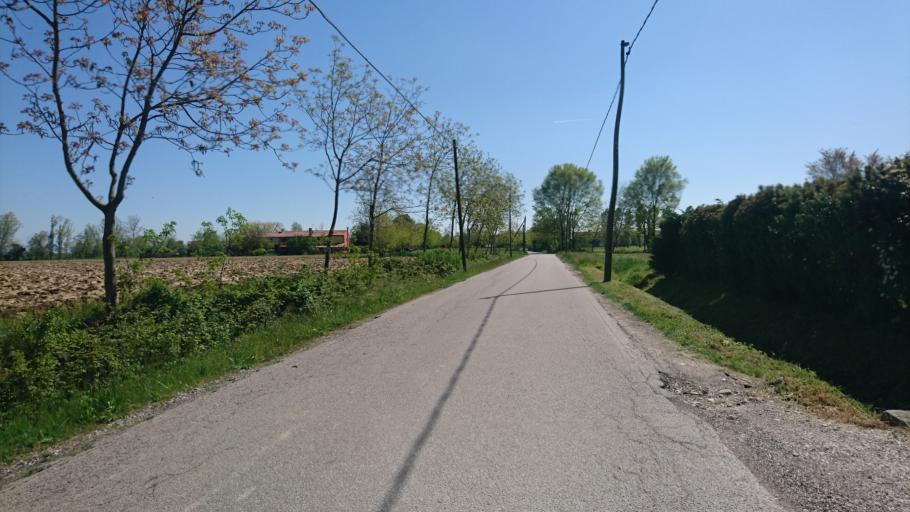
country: IT
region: Veneto
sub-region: Provincia di Venezia
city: Marcon-Gaggio-Colmello
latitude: 45.5859
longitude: 12.2784
